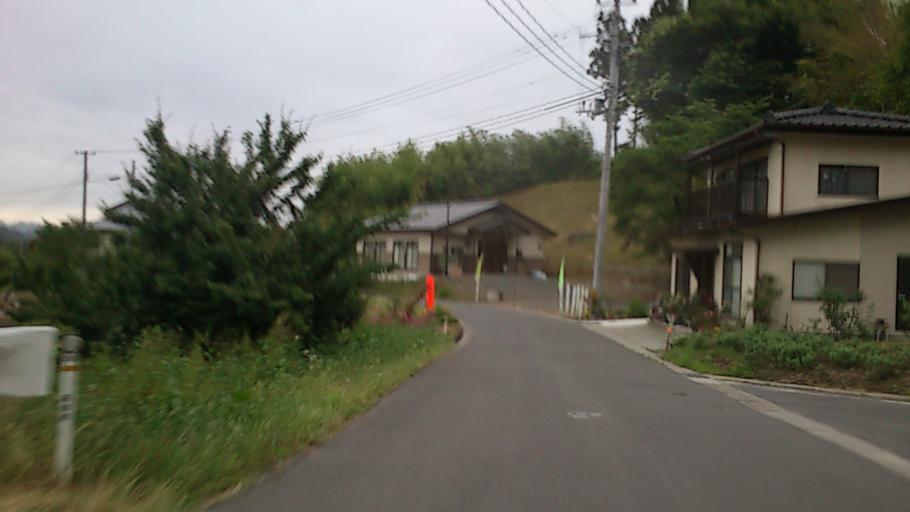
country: JP
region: Fukushima
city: Fukushima-shi
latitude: 37.6656
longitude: 140.5061
